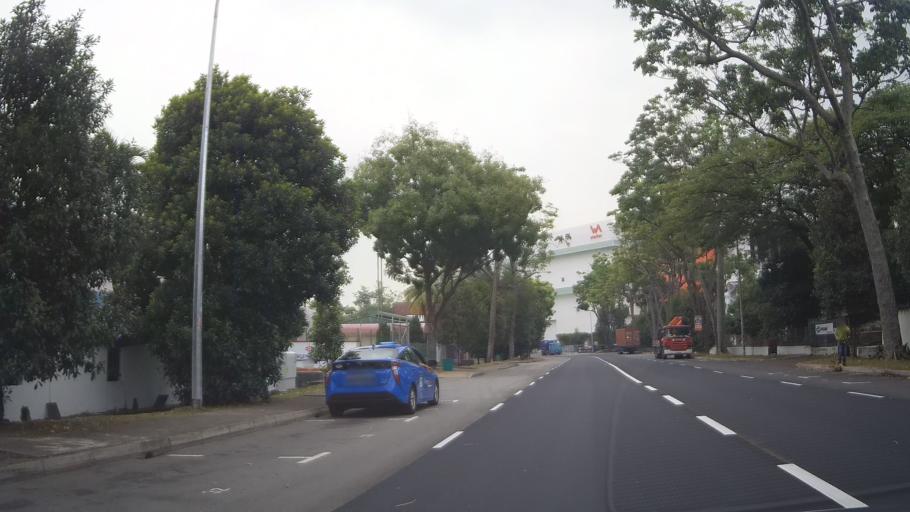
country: MY
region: Johor
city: Johor Bahru
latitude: 1.3147
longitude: 103.6678
